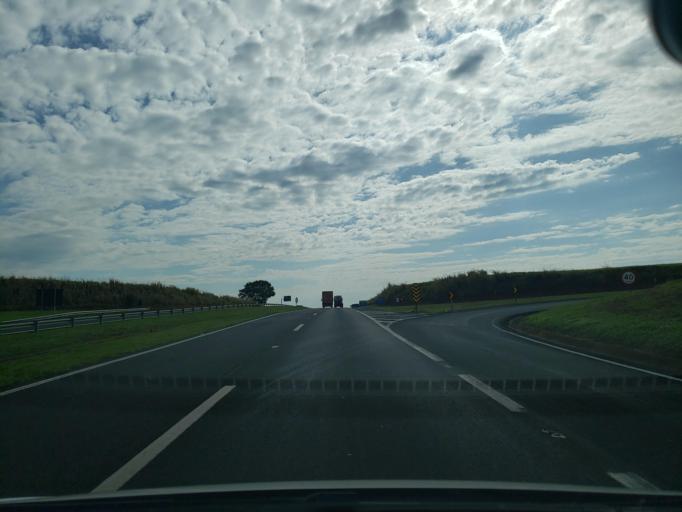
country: BR
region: Sao Paulo
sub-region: Lins
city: Lins
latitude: -21.6652
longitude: -49.7903
